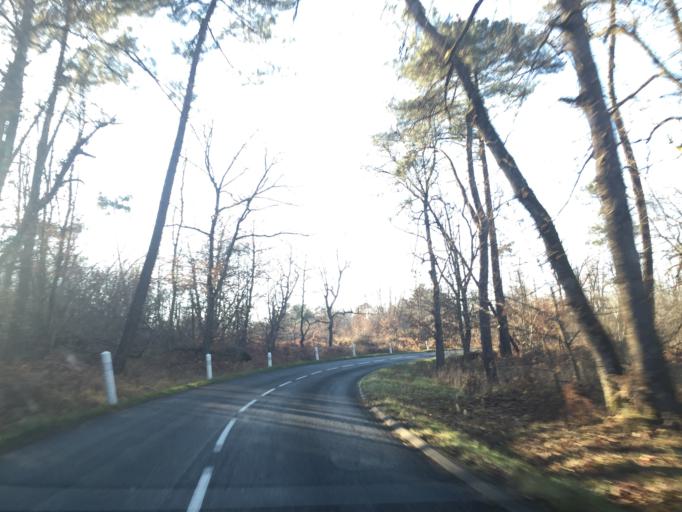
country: FR
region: Aquitaine
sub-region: Departement de la Dordogne
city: Neuvic
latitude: 45.1457
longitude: 0.4295
